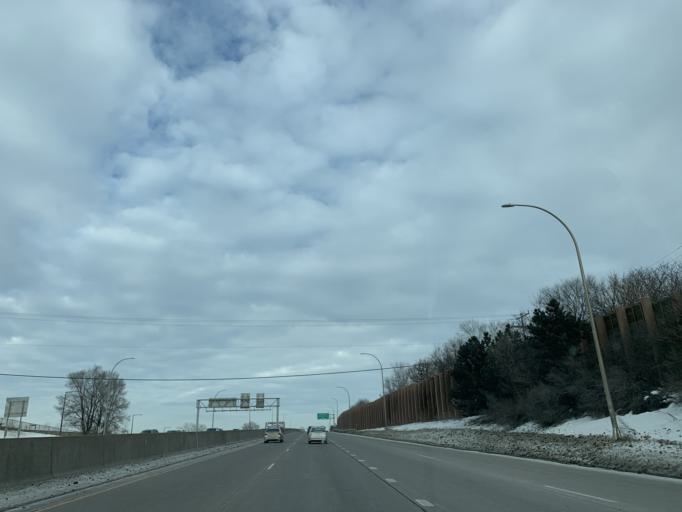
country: US
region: Minnesota
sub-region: Ramsey County
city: Lauderdale
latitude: 44.9694
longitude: -93.2022
